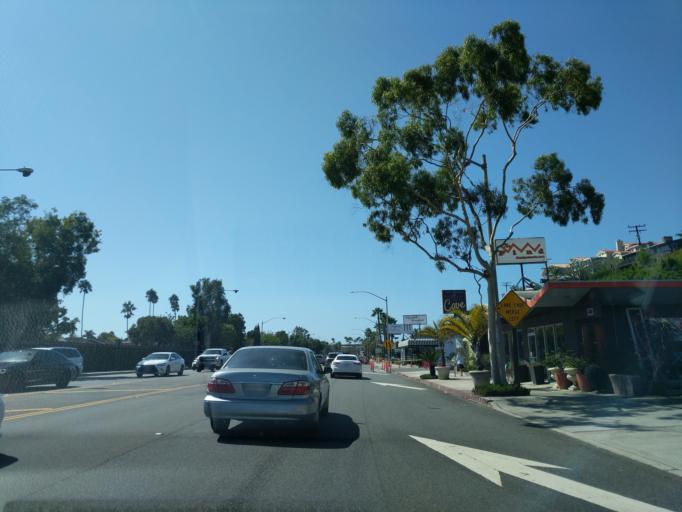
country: US
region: California
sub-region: Orange County
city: Newport Beach
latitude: 33.6162
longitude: -117.9086
